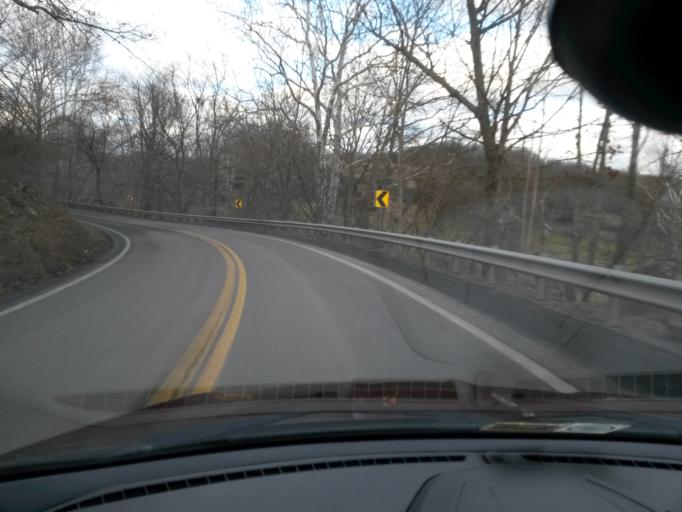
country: US
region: West Virginia
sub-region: Monroe County
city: Union
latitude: 37.5586
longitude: -80.5689
